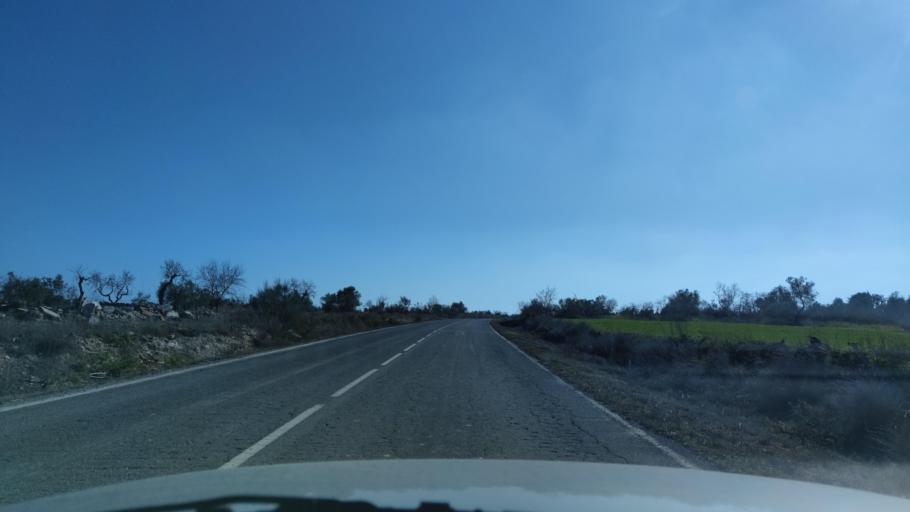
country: ES
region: Catalonia
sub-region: Provincia de Lleida
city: Maials
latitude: 41.3230
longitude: 0.4231
